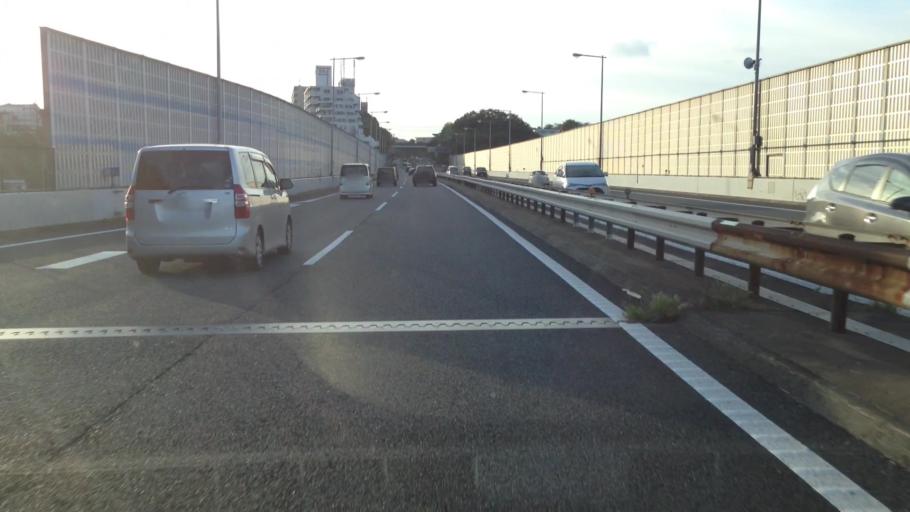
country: JP
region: Kanagawa
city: Kamakura
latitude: 35.3849
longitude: 139.5814
